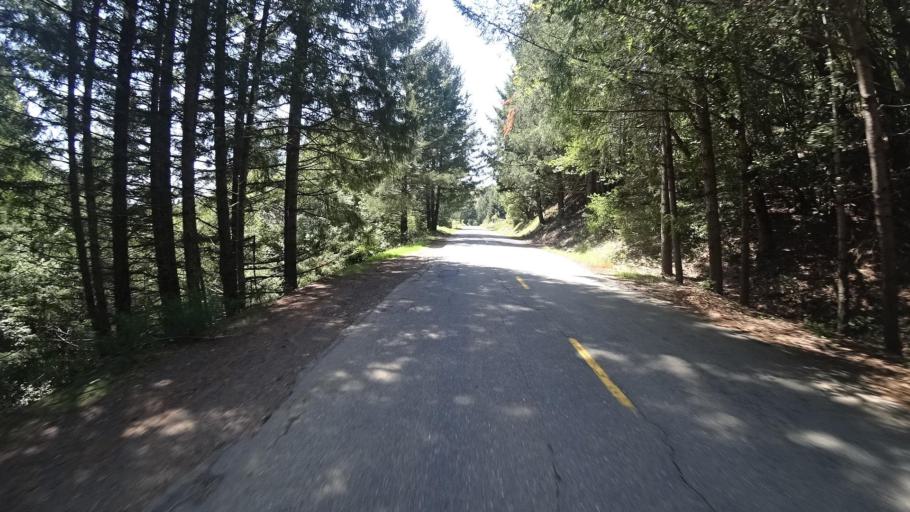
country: US
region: California
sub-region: Humboldt County
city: Redway
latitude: 40.1181
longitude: -123.6714
